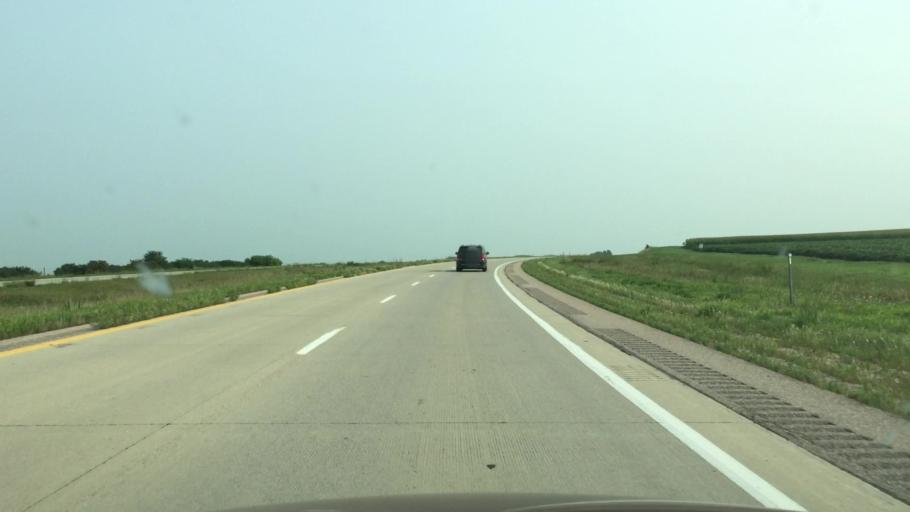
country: US
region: Iowa
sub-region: O'Brien County
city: Sheldon
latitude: 43.1073
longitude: -95.8981
